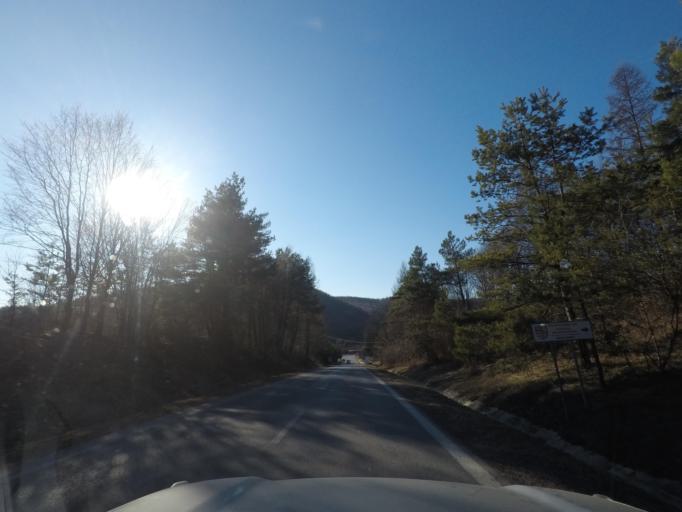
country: SK
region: Presovsky
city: Medzilaborce
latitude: 49.2527
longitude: 21.9152
